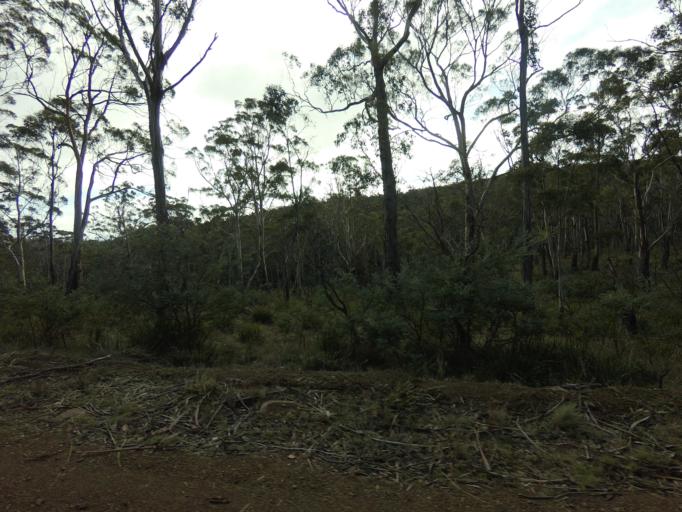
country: AU
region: Tasmania
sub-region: Derwent Valley
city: New Norfolk
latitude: -42.7587
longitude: 146.8878
